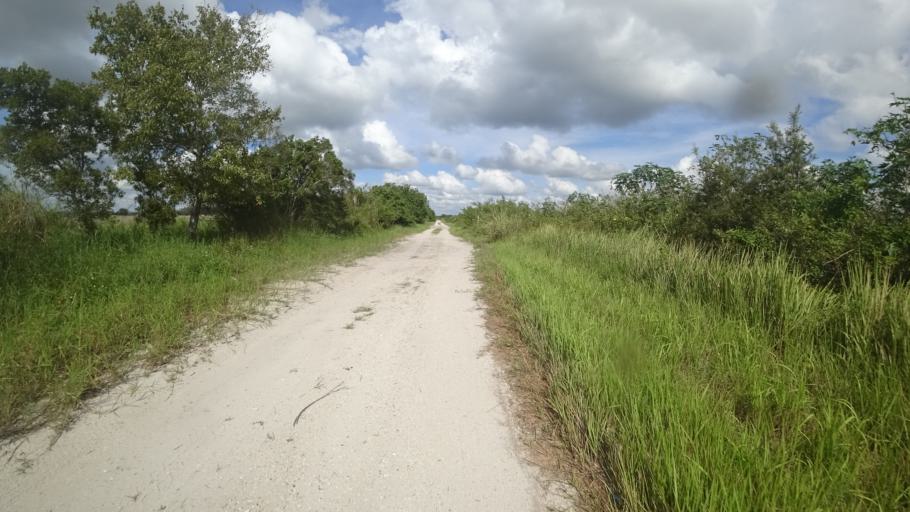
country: US
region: Florida
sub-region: Hillsborough County
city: Wimauma
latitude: 27.5823
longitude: -82.2672
